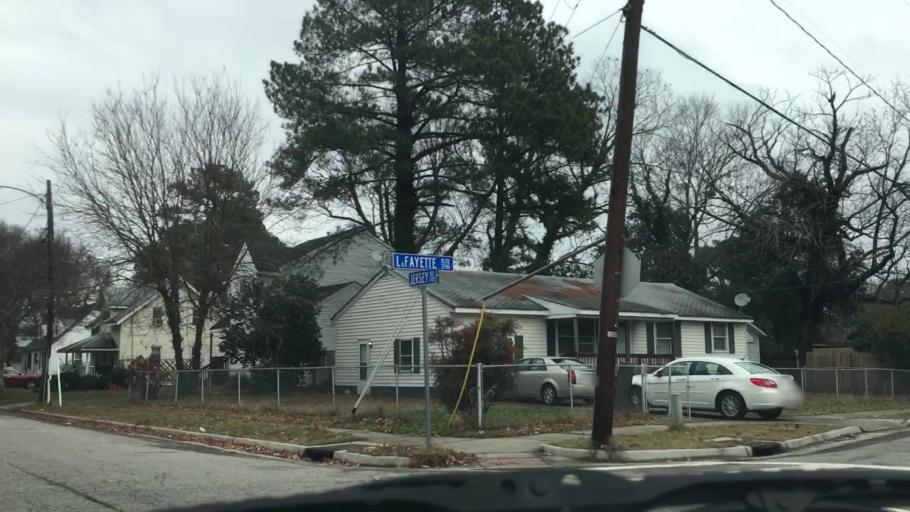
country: US
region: Virginia
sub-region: City of Norfolk
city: Norfolk
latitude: 36.8758
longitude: -76.2467
